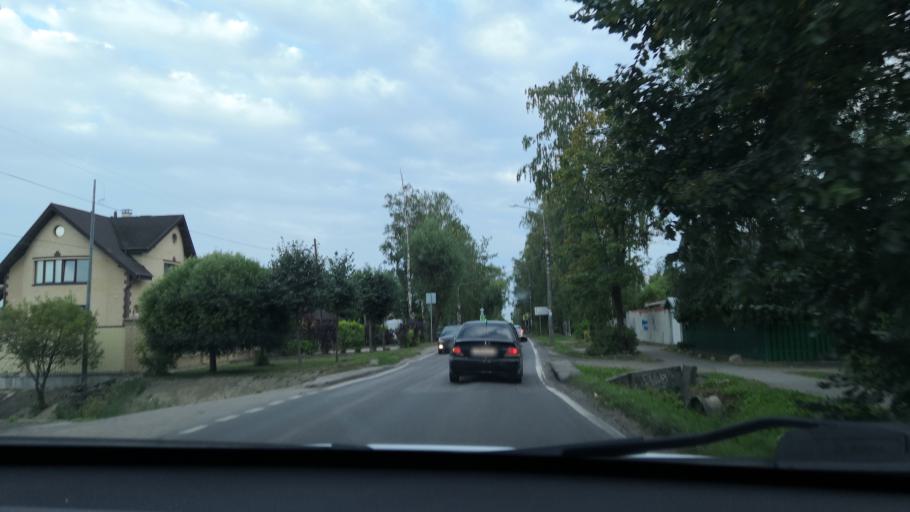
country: RU
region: St.-Petersburg
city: Pushkin
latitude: 59.7004
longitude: 30.4090
